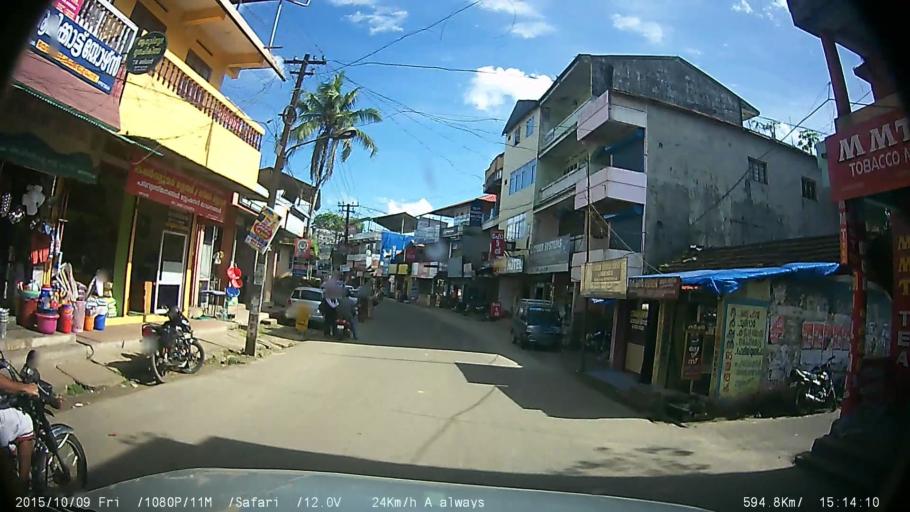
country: IN
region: Kerala
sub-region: Ernakulam
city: Piravam
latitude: 9.8632
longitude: 76.5937
